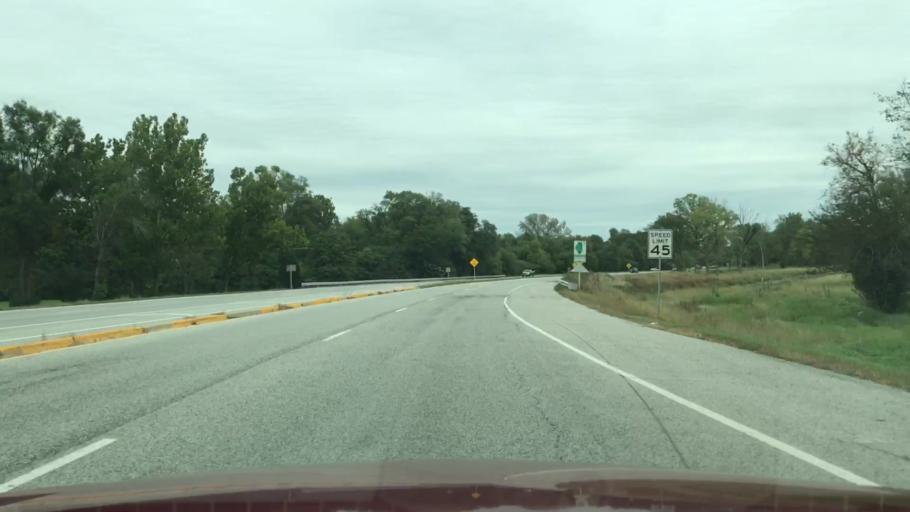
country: US
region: Illinois
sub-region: DuPage County
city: Lisle
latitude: 41.8180
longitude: -88.0705
